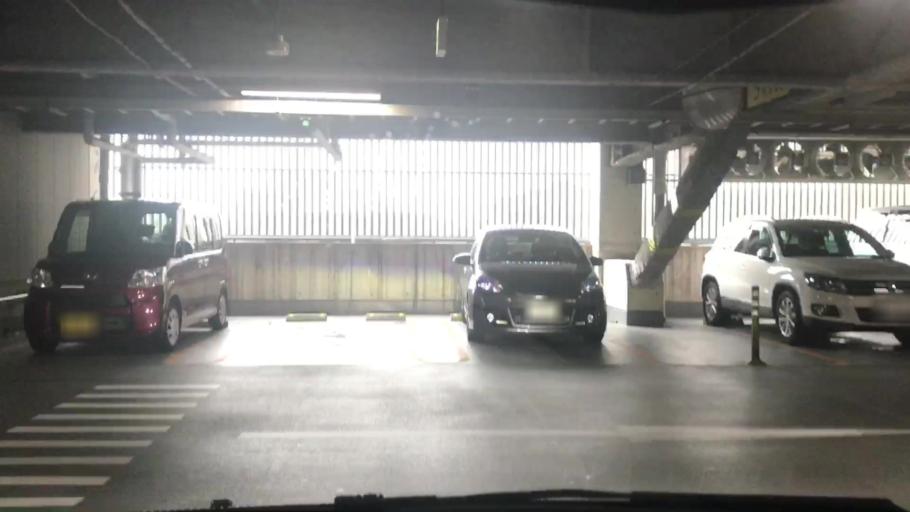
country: JP
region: Hyogo
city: Nishinomiya-hama
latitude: 34.7436
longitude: 135.3594
